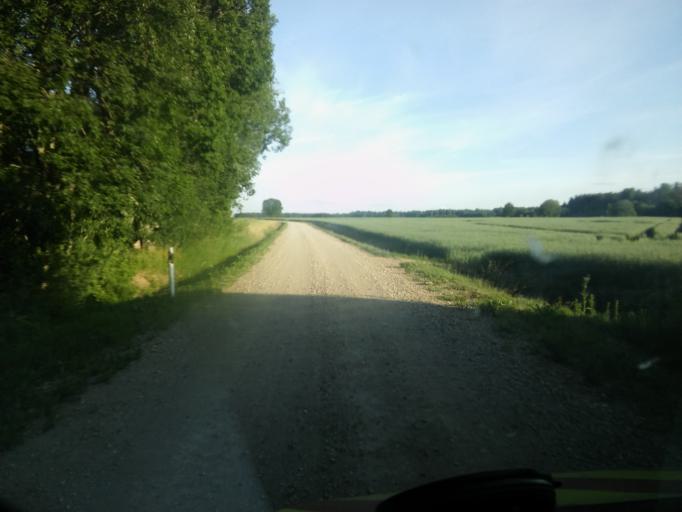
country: EE
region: Valgamaa
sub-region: Torva linn
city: Torva
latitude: 58.0714
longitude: 25.9024
